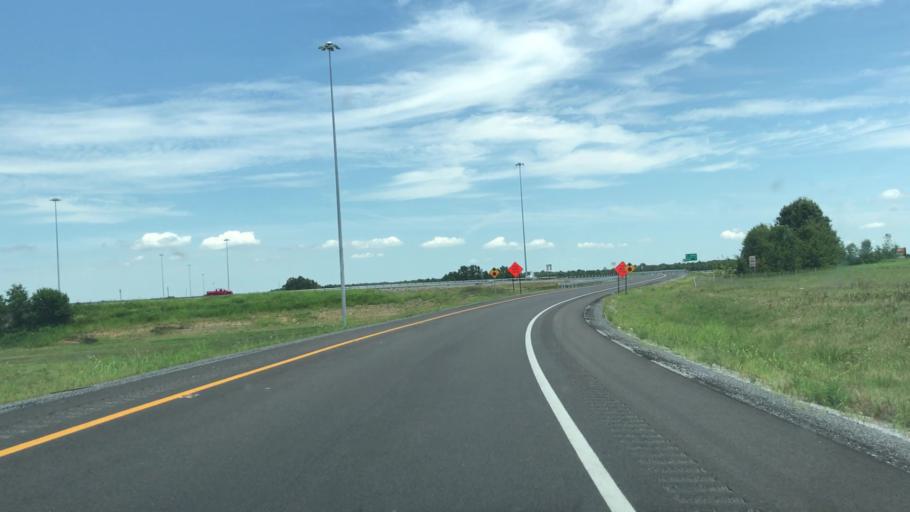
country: US
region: Kentucky
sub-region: Marshall County
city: Benton
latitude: 36.8669
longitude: -88.3653
